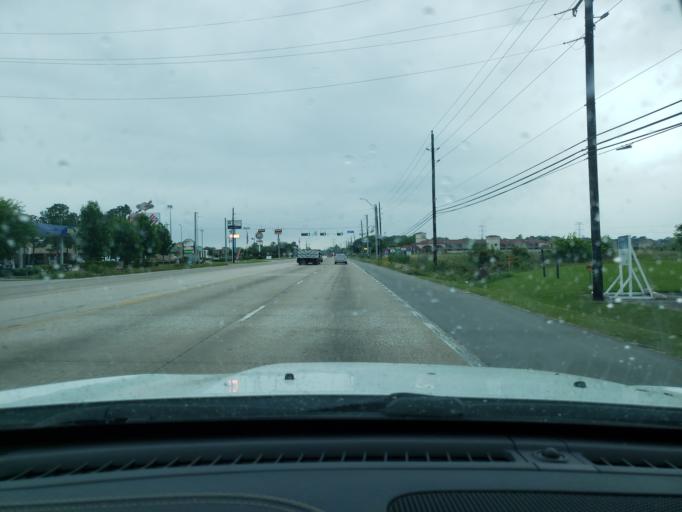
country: US
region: Texas
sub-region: Chambers County
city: Mont Belvieu
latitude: 29.8107
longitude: -94.9023
